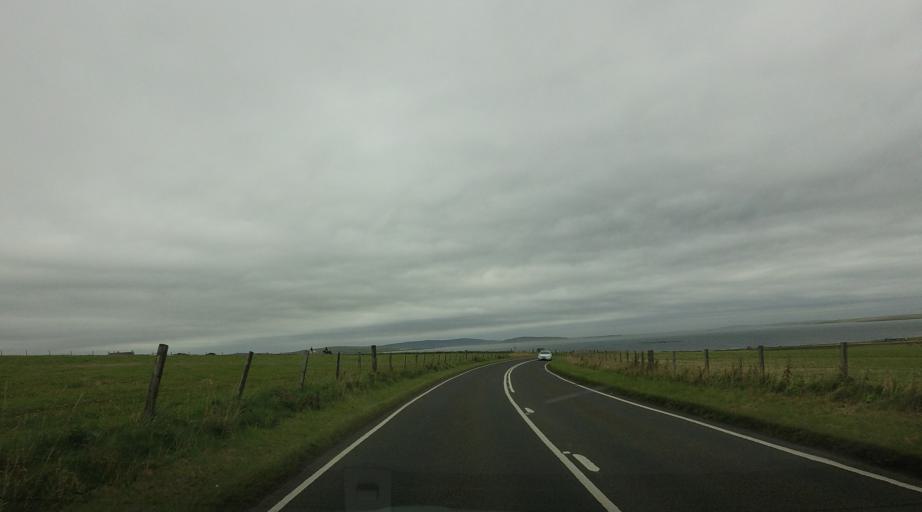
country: GB
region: Scotland
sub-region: Orkney Islands
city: Orkney
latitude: 58.9942
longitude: -2.9941
